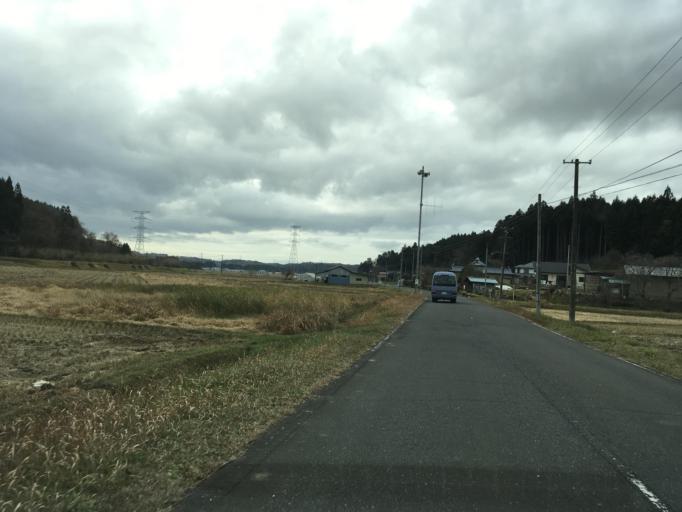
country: JP
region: Iwate
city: Ichinoseki
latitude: 38.8263
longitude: 141.0489
